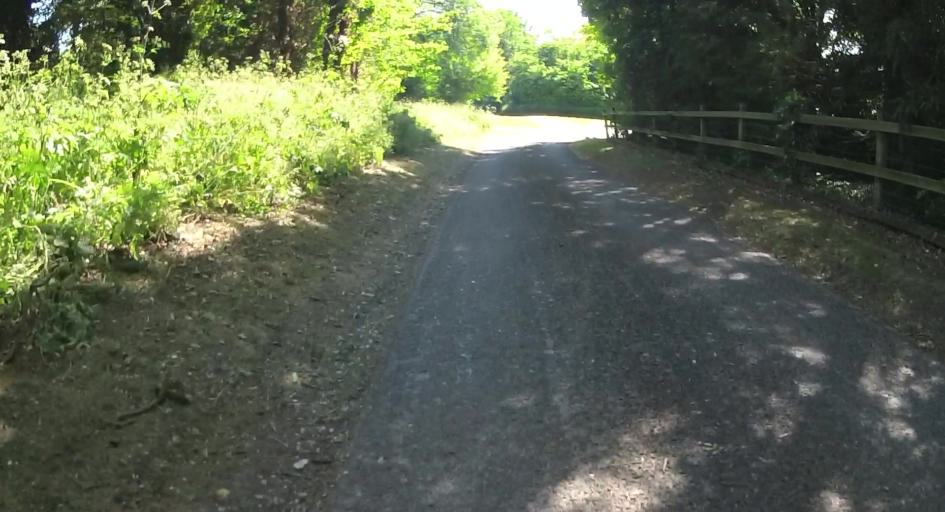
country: GB
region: England
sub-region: Hampshire
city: Kingsclere
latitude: 51.2973
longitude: -1.2963
